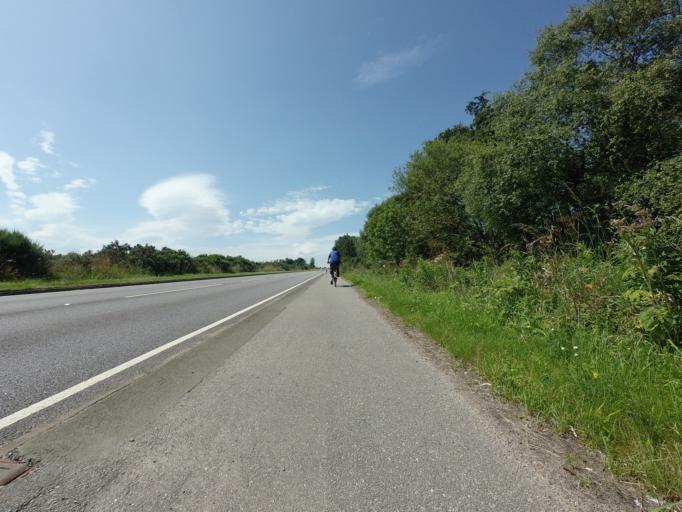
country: GB
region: Scotland
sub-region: Highland
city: Conon Bridge
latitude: 57.5390
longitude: -4.3551
